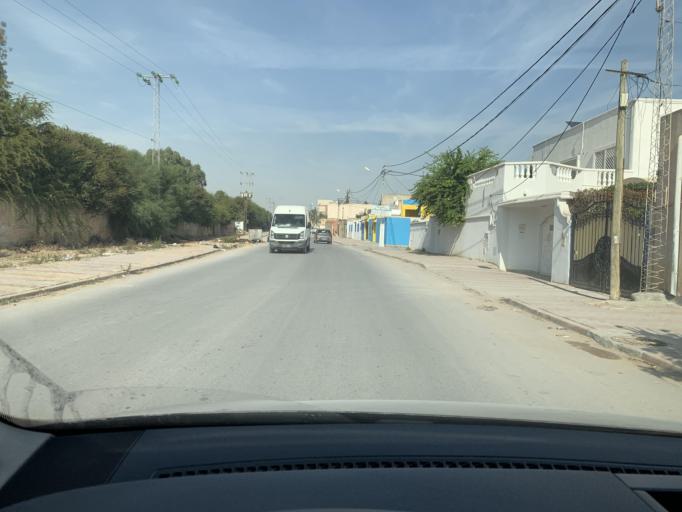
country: TN
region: Manouba
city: Manouba
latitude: 36.8173
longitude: 10.1176
